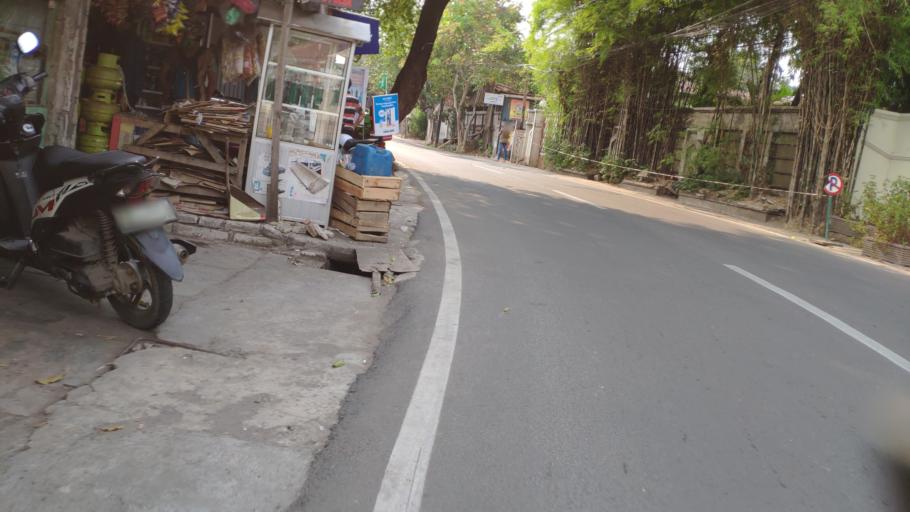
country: ID
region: West Java
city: Pamulang
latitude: -6.3162
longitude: 106.8142
